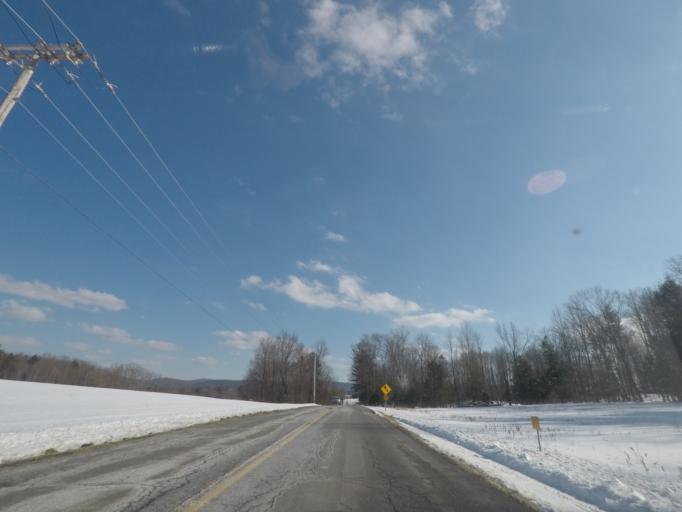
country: US
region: New York
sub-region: Rensselaer County
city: Hoosick Falls
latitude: 42.8505
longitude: -73.4916
